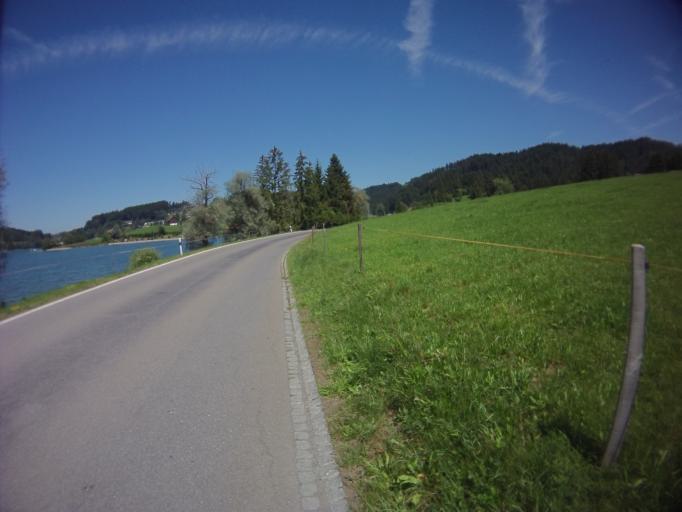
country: CH
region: Schwyz
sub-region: Bezirk Einsiedeln
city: Einsiedeln
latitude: 47.1471
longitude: 8.7908
